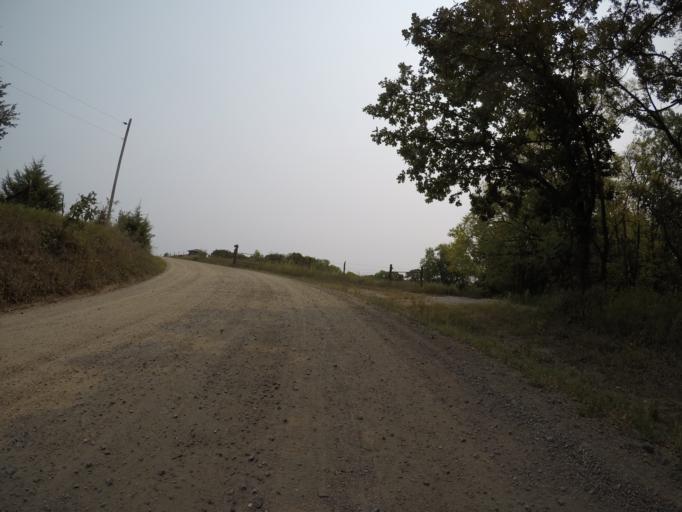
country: US
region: Kansas
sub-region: Marshall County
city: Marysville
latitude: 39.8567
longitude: -96.6521
